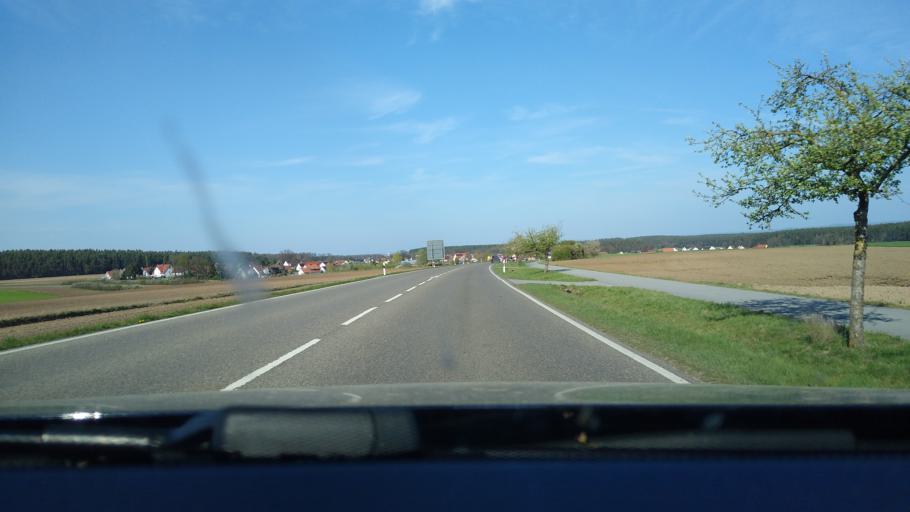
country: DE
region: Bavaria
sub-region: Regierungsbezirk Mittelfranken
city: Kammerstein
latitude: 49.2986
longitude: 10.9787
